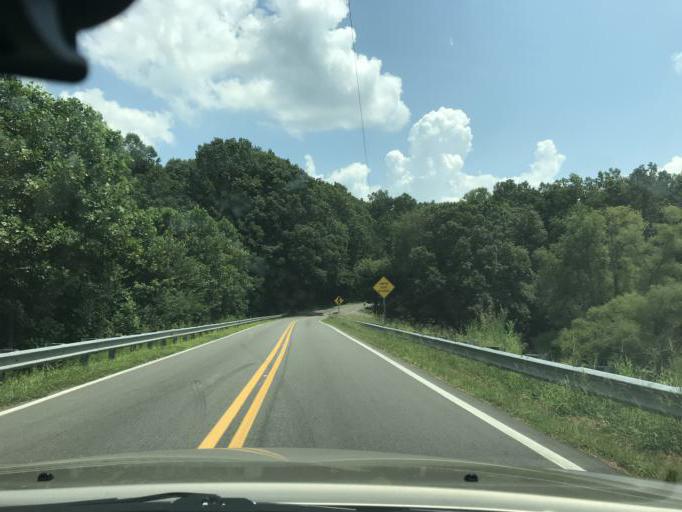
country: US
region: Georgia
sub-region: Forsyth County
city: Cumming
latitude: 34.2656
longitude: -84.2283
